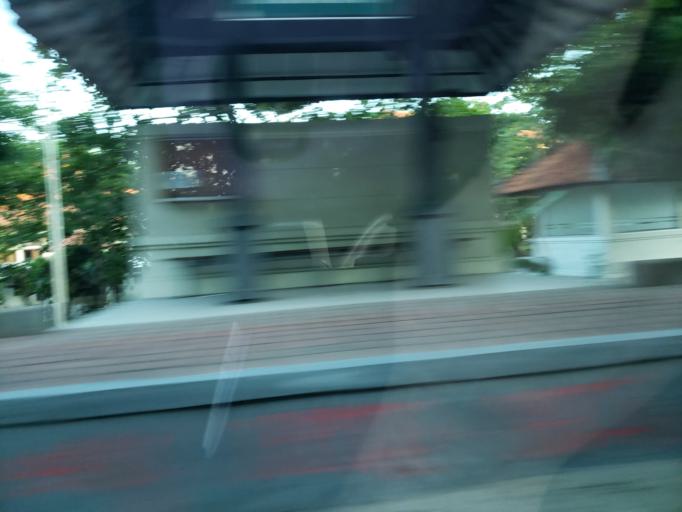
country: ID
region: Bali
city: Jimbaran
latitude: -8.7957
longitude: 115.1756
